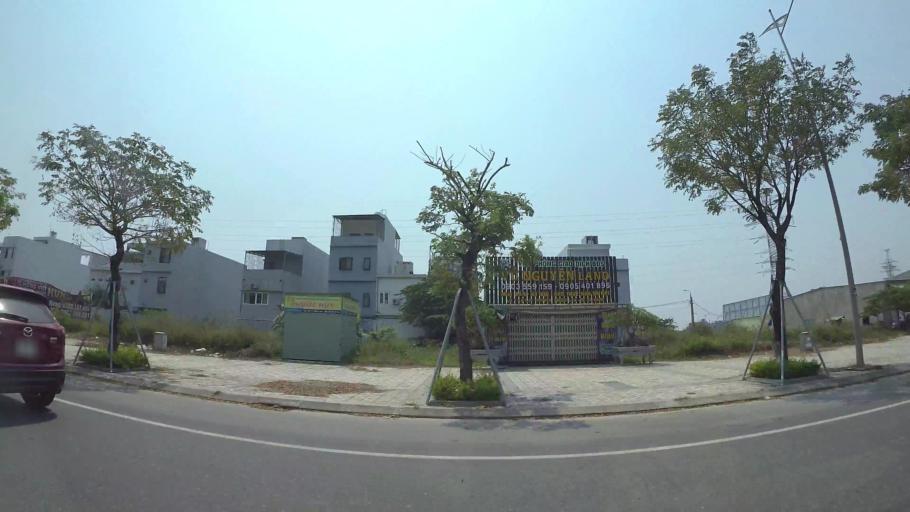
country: VN
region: Da Nang
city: Ngu Hanh Son
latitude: 16.0179
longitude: 108.2312
